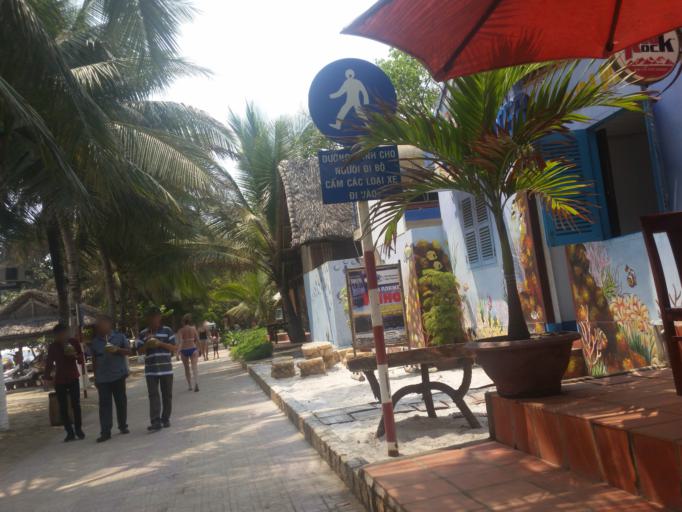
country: VN
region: Khanh Hoa
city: Nha Trang
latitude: 12.2293
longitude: 109.1997
